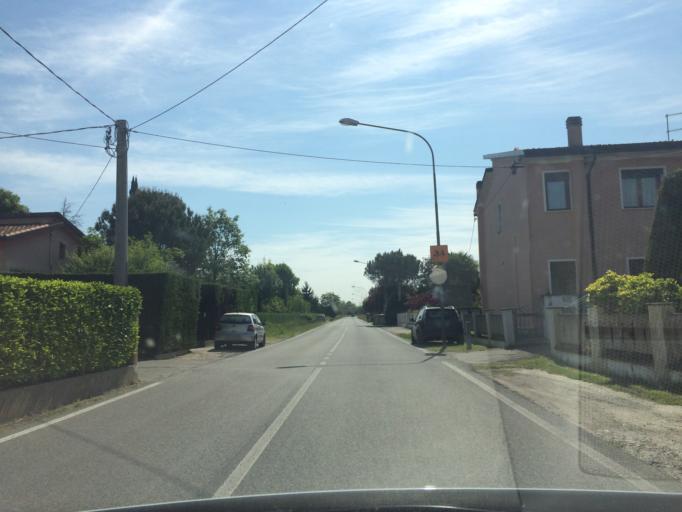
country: IT
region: Veneto
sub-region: Provincia di Padova
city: Abano Terme
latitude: 45.3517
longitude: 11.7983
